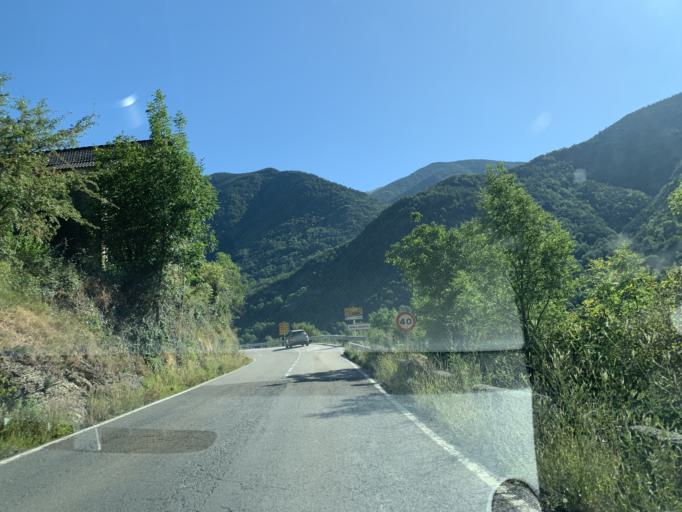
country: ES
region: Aragon
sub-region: Provincia de Huesca
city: Broto
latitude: 42.6238
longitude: -0.1133
